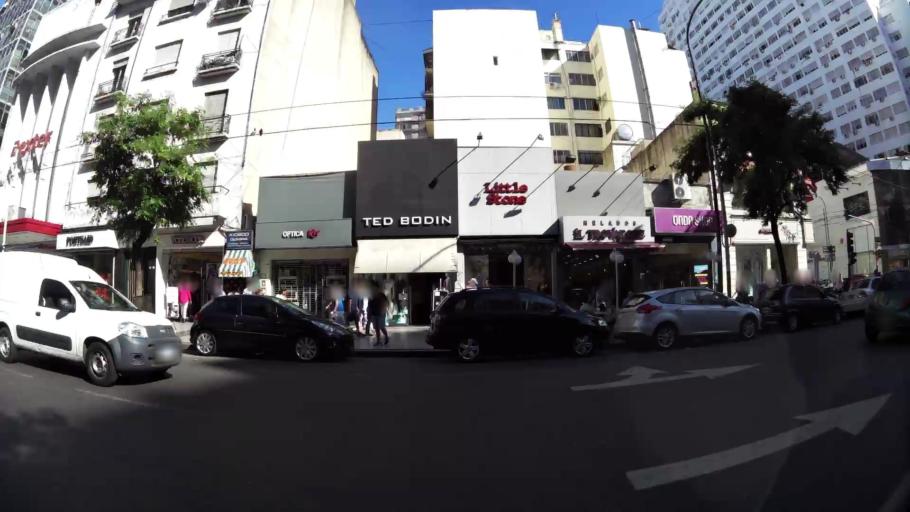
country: AR
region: Buenos Aires F.D.
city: Villa Santa Rita
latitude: -34.6188
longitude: -58.4375
